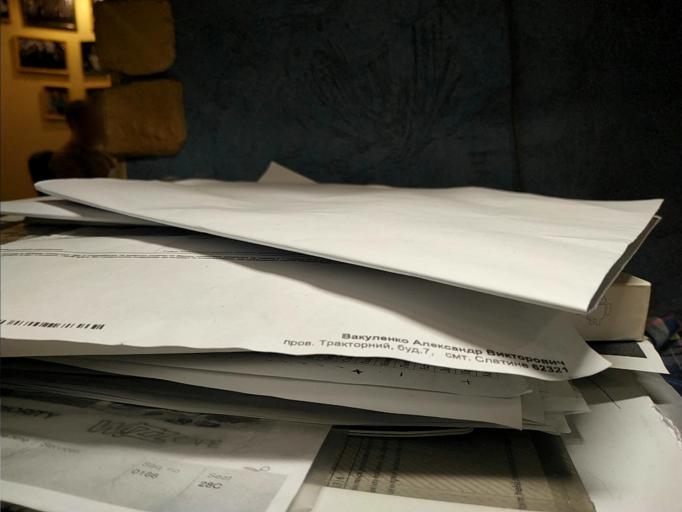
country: RU
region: Tverskaya
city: Zubtsov
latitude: 56.1289
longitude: 34.5236
